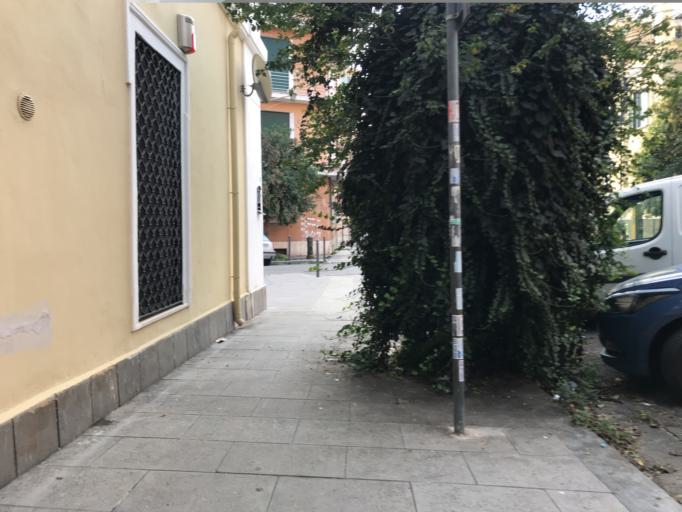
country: IT
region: Latium
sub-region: Citta metropolitana di Roma Capitale
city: Rome
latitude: 41.9103
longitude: 12.5168
